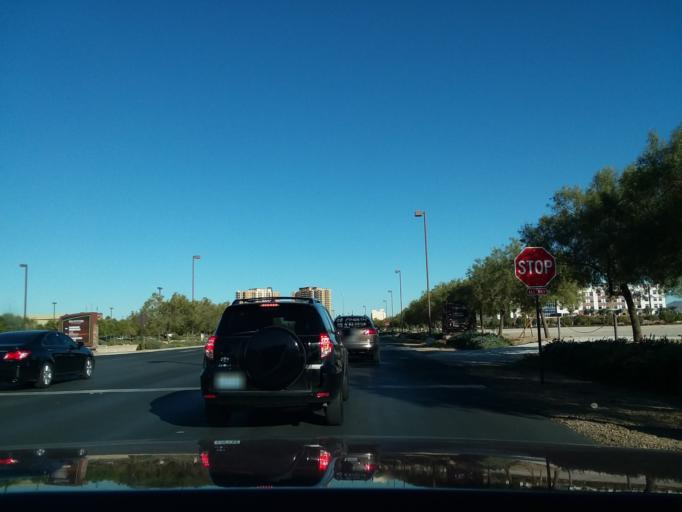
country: US
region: Nevada
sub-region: Clark County
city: Enterprise
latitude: 36.0388
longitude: -115.1865
